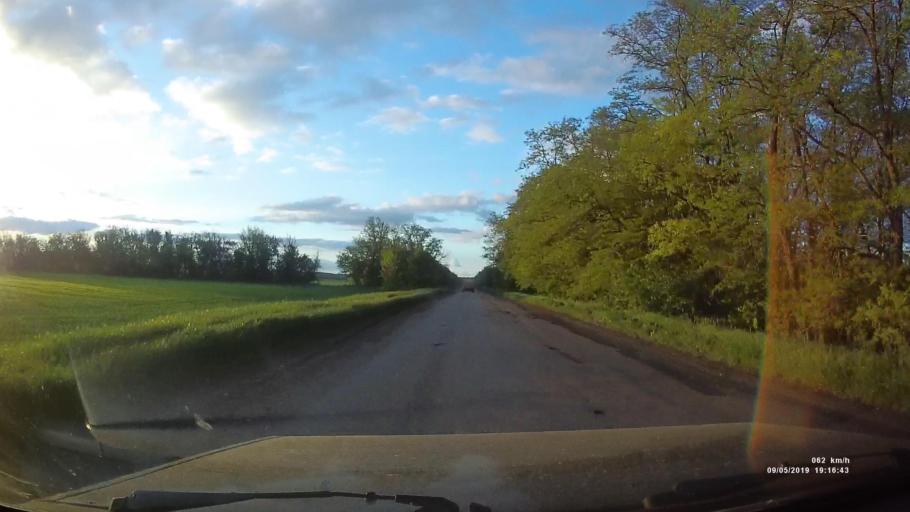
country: RU
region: Krasnodarskiy
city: Kanelovskaya
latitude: 46.7801
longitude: 39.2116
